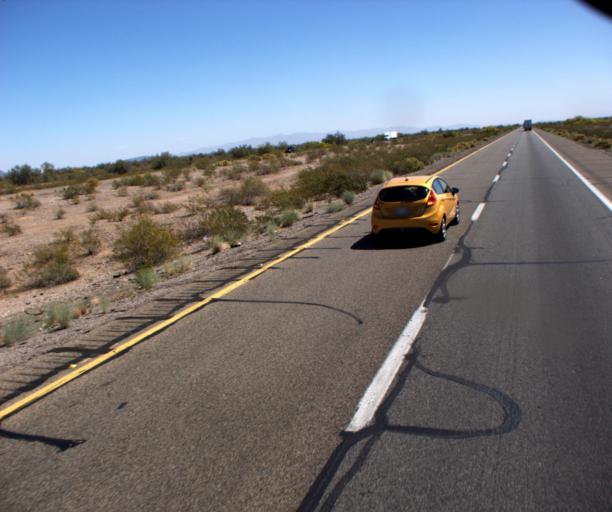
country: US
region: Arizona
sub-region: Maricopa County
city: Buckeye
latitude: 33.5091
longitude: -113.0039
